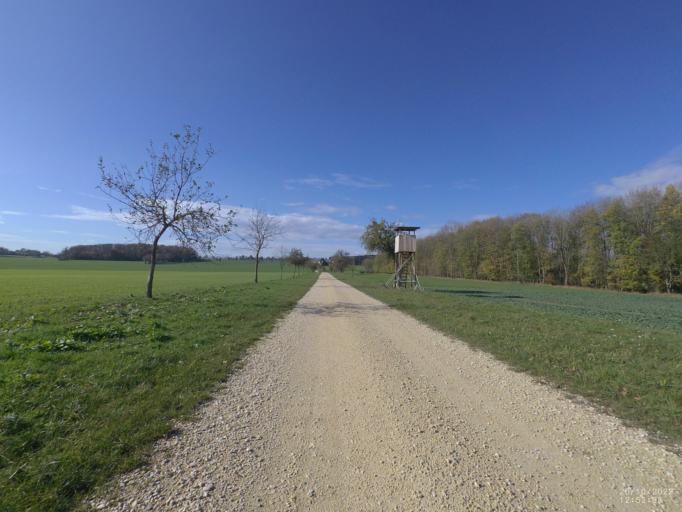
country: DE
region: Baden-Wuerttemberg
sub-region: Regierungsbezirk Stuttgart
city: Donzdorf
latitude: 48.6882
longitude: 9.8516
